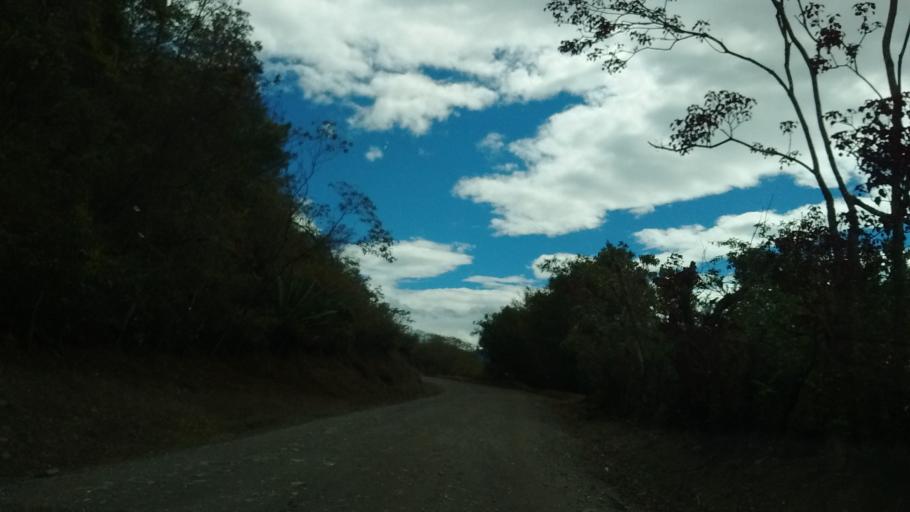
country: CO
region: Cauca
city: Almaguer
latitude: 1.8528
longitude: -76.9278
